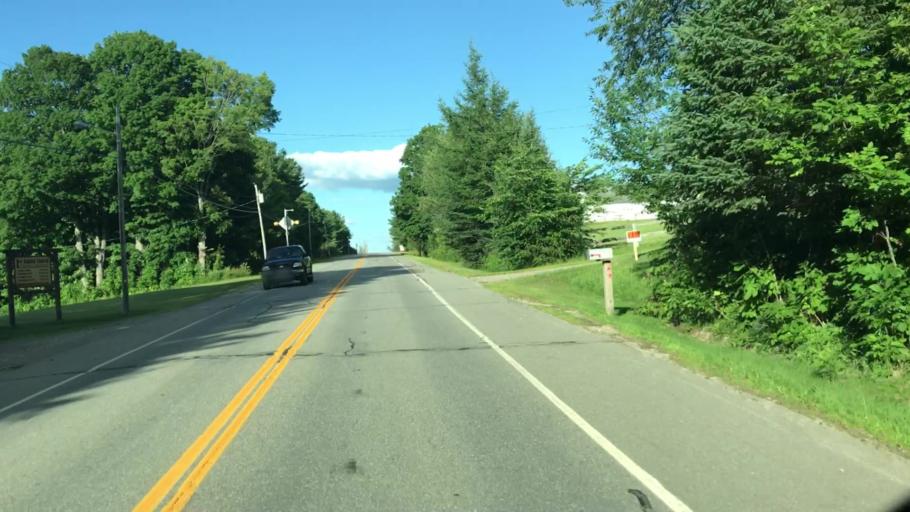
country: US
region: Maine
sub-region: Penobscot County
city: Lincoln
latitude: 45.3596
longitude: -68.2762
